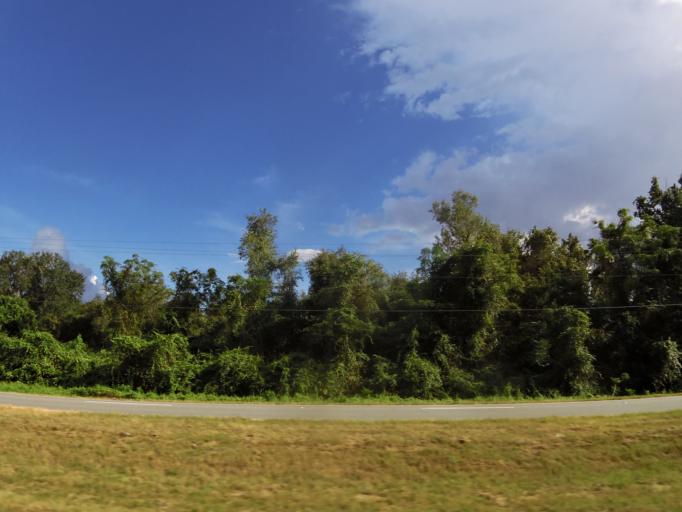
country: US
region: Georgia
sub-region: Lowndes County
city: Remerton
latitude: 30.8042
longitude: -83.3611
